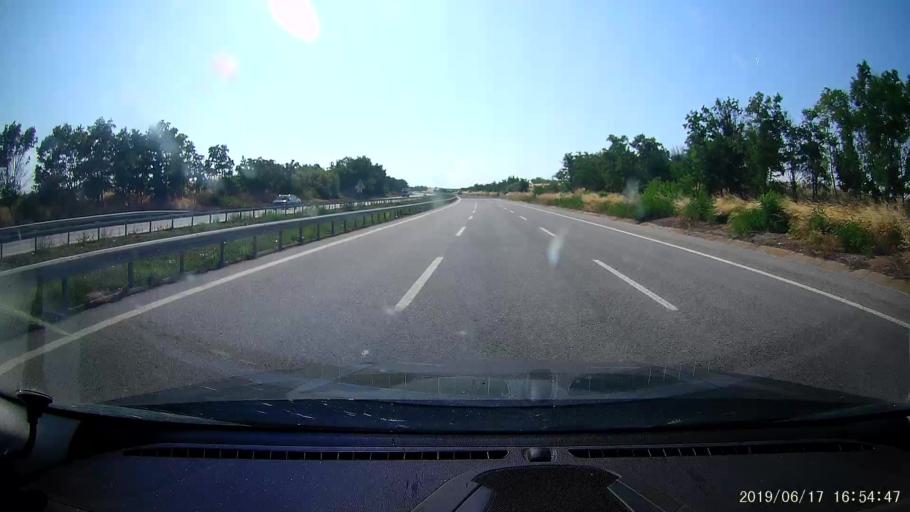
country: TR
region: Kirklareli
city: Inece
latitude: 41.5767
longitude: 26.9851
